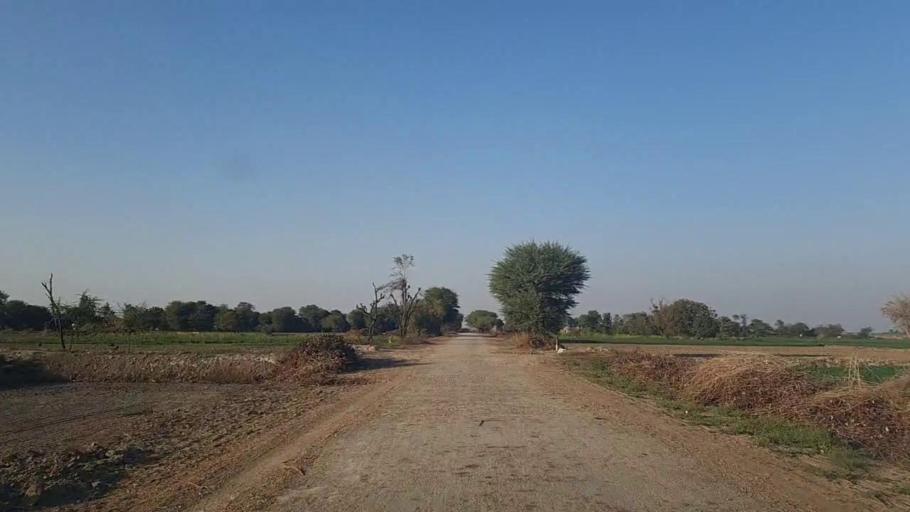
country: PK
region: Sindh
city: Jam Sahib
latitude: 26.3050
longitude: 68.6704
